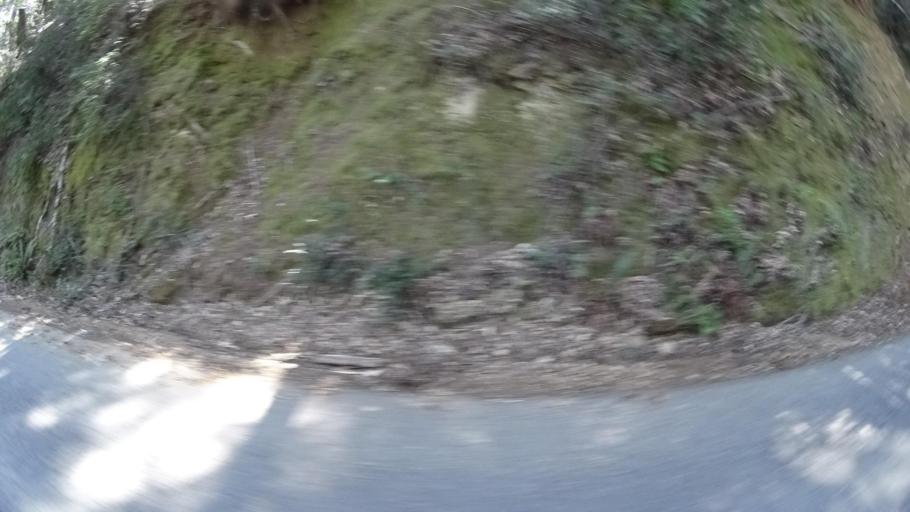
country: US
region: California
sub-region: Humboldt County
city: Redway
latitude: 40.0982
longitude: -123.9503
